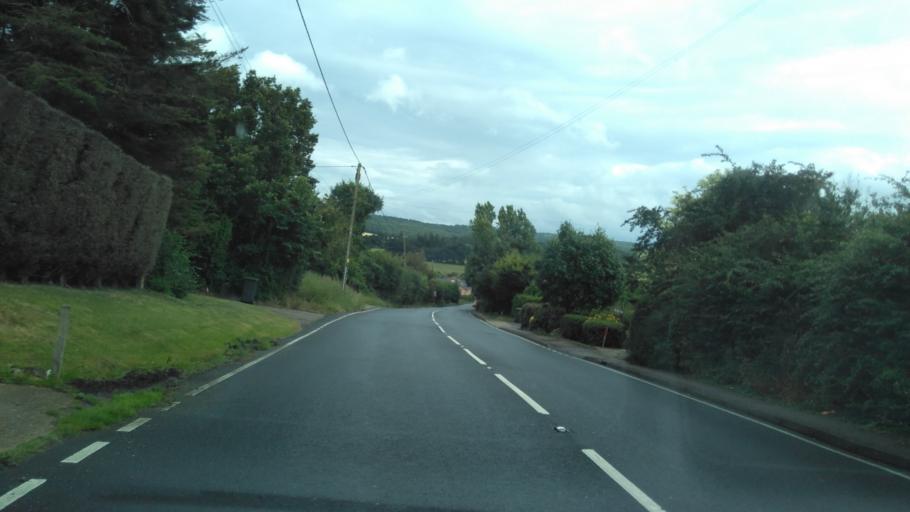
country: GB
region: England
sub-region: Kent
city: Whitstable
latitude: 51.3362
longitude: 1.0219
